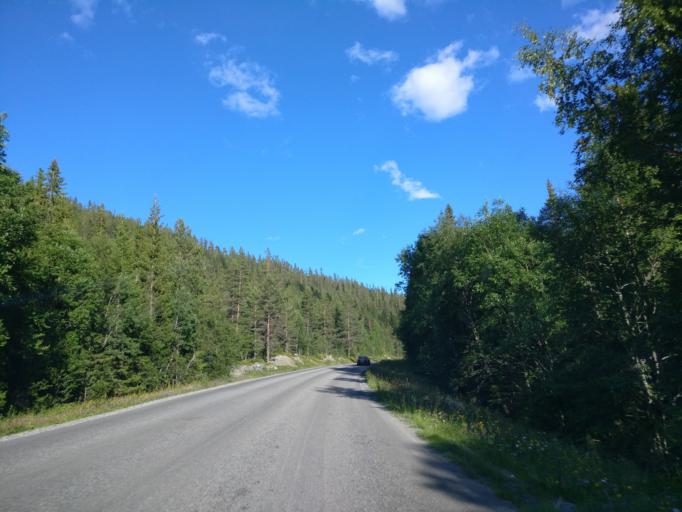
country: SE
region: Jaemtland
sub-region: Bergs Kommun
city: Hoverberg
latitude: 62.4904
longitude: 13.9565
